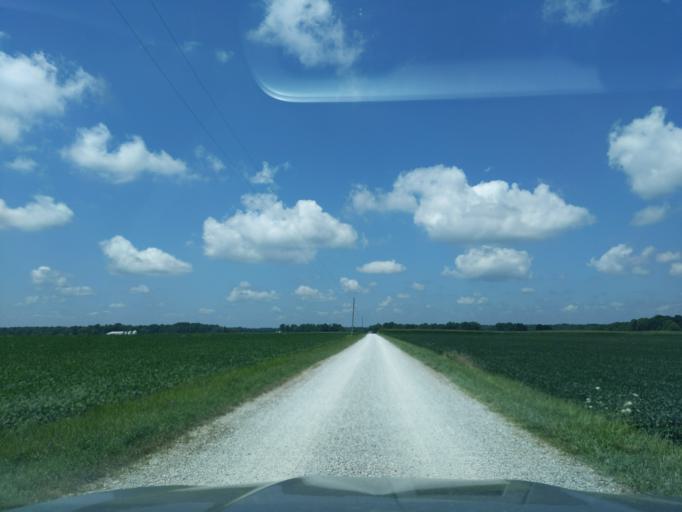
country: US
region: Indiana
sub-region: Ripley County
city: Osgood
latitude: 39.2205
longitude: -85.3771
